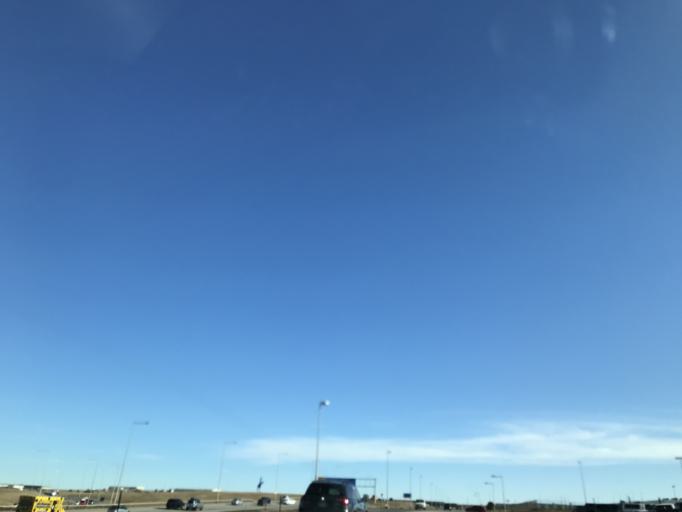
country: US
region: Colorado
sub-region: Weld County
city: Lochbuie
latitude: 39.8329
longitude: -104.6810
